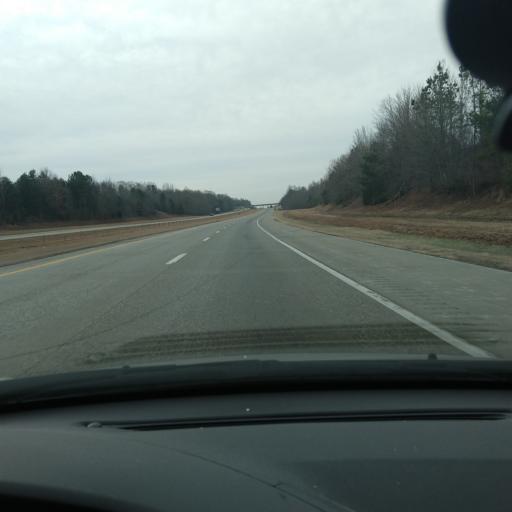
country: US
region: North Carolina
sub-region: Davidson County
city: Midway
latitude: 35.9272
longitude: -80.2316
